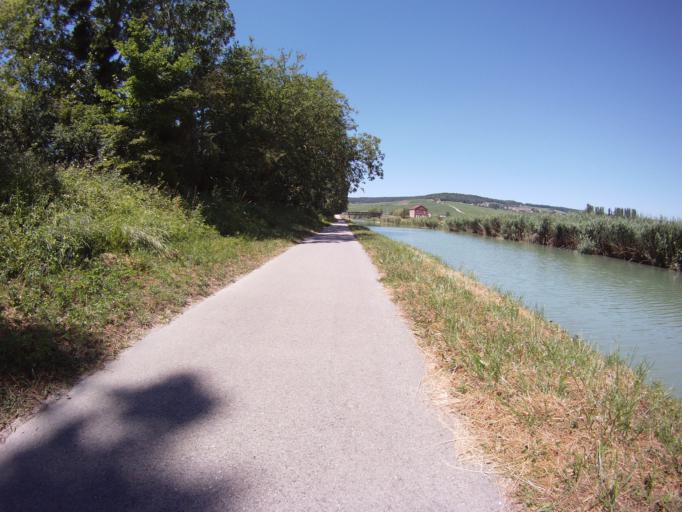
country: FR
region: Champagne-Ardenne
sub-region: Departement de la Marne
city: Dizy
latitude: 49.0658
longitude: 3.9516
